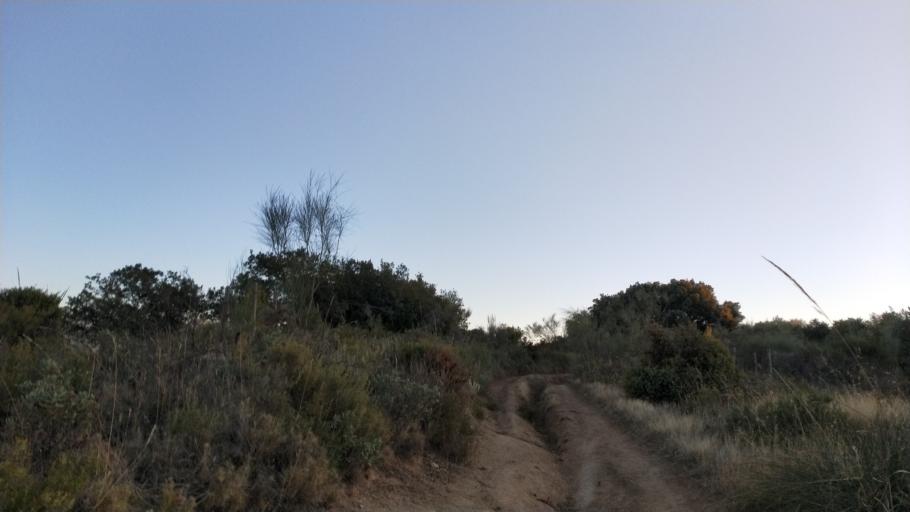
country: ES
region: Andalusia
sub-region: Provincia de Granada
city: Dudar
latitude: 37.2016
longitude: -3.5018
